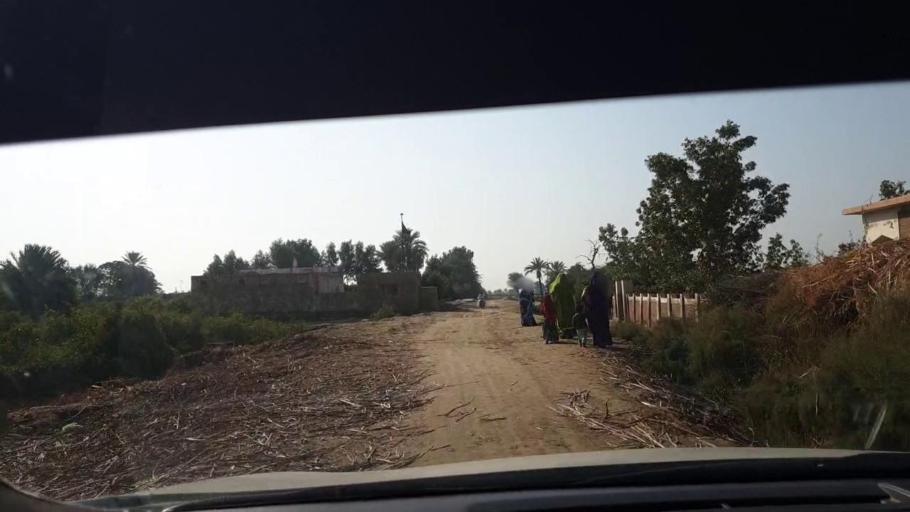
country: PK
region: Sindh
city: Berani
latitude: 25.8007
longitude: 68.8953
